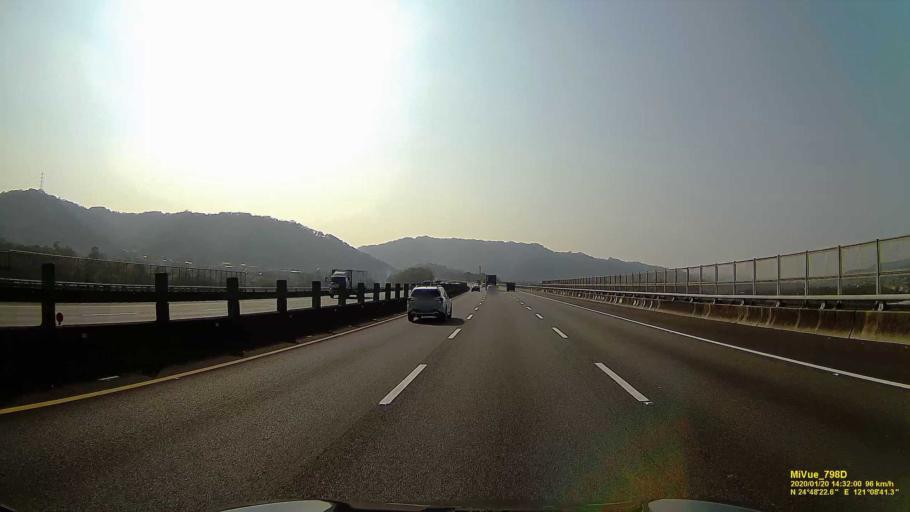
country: TW
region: Taiwan
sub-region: Hsinchu
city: Zhubei
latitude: 24.8063
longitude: 121.1441
